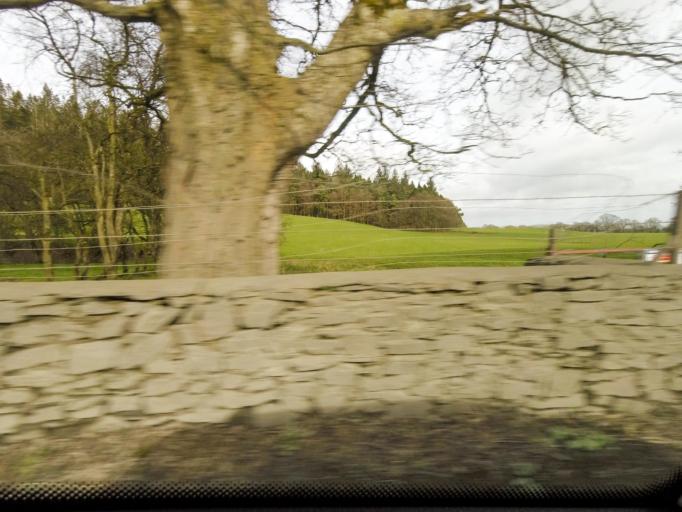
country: IE
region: Leinster
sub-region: Wicklow
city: Blessington
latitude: 53.1765
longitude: -6.5591
